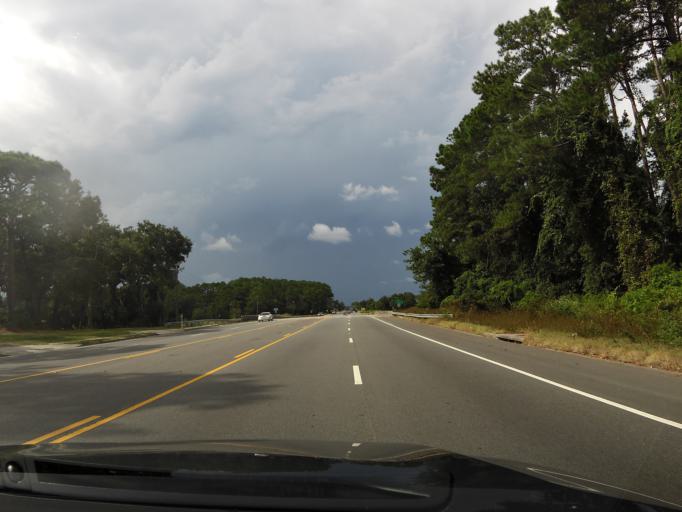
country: US
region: Georgia
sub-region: Glynn County
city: Dock Junction
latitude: 31.2329
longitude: -81.5344
